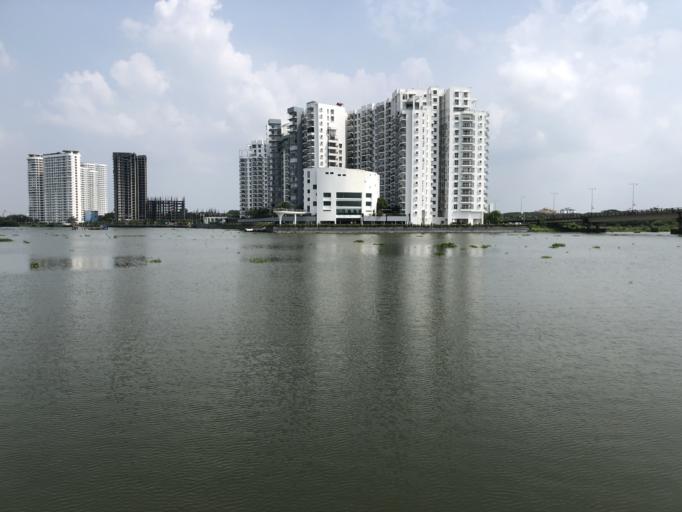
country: IN
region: Kerala
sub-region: Ernakulam
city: Cochin
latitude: 9.9934
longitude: 76.2666
